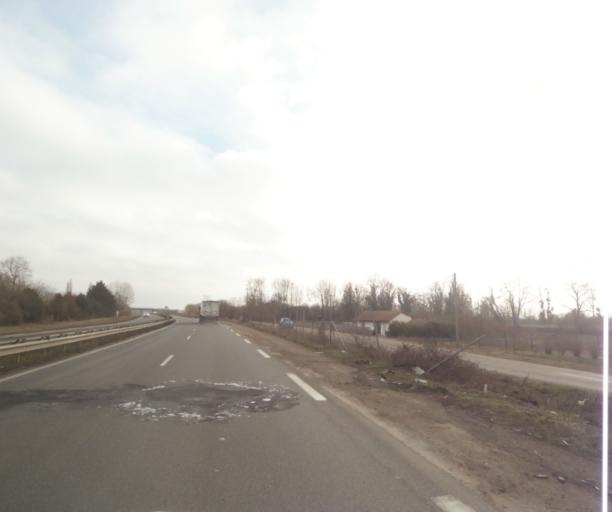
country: FR
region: Champagne-Ardenne
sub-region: Departement de la Haute-Marne
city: Villiers-en-Lieu
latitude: 48.6540
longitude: 4.8215
